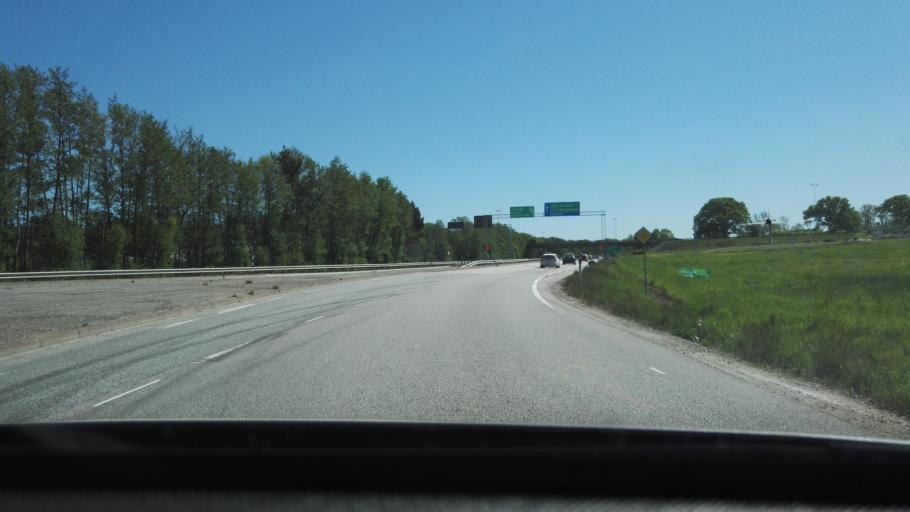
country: SE
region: Blekinge
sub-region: Ronneby Kommun
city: Kallinge
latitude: 56.2325
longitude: 15.2595
